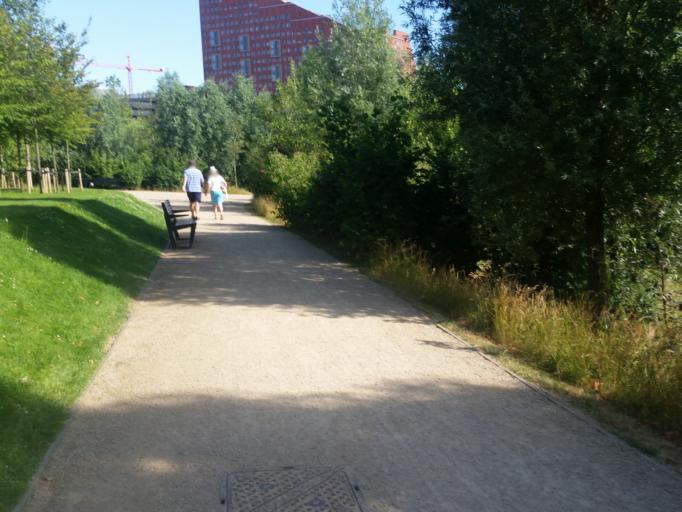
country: GB
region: England
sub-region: Greater London
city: Poplar
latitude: 51.5465
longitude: -0.0140
